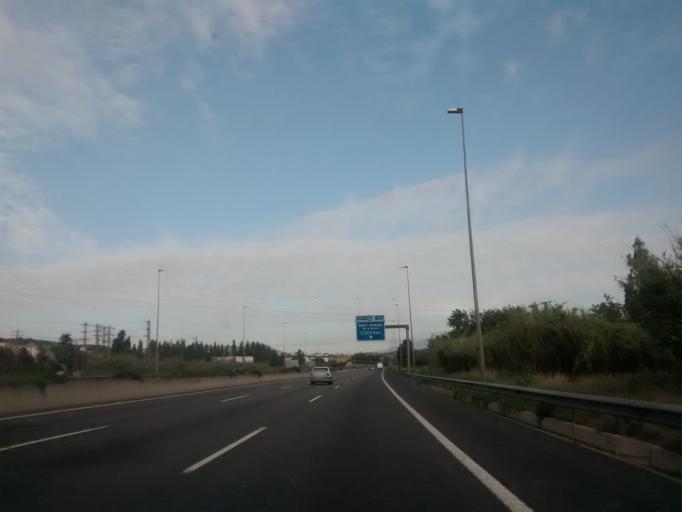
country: ES
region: Catalonia
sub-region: Provincia de Barcelona
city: Sant Andreu de la Barca
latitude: 41.4420
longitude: 1.9854
